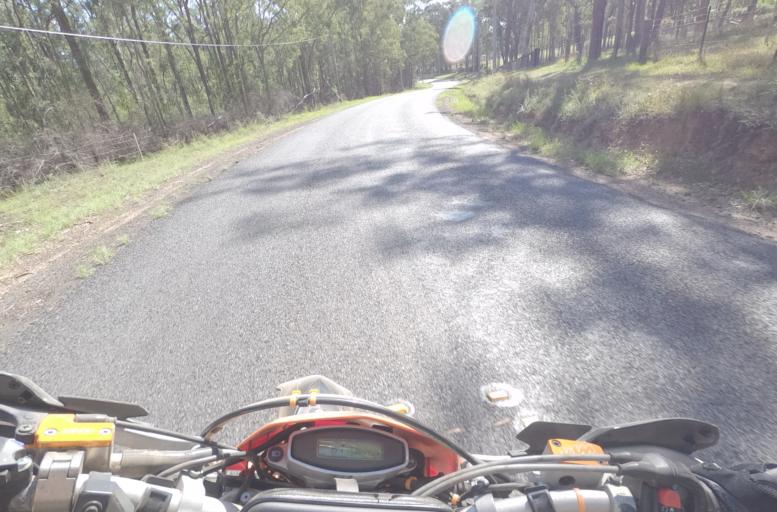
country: AU
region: New South Wales
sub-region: Hawkesbury
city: Scheyville
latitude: -33.5867
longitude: 150.9031
